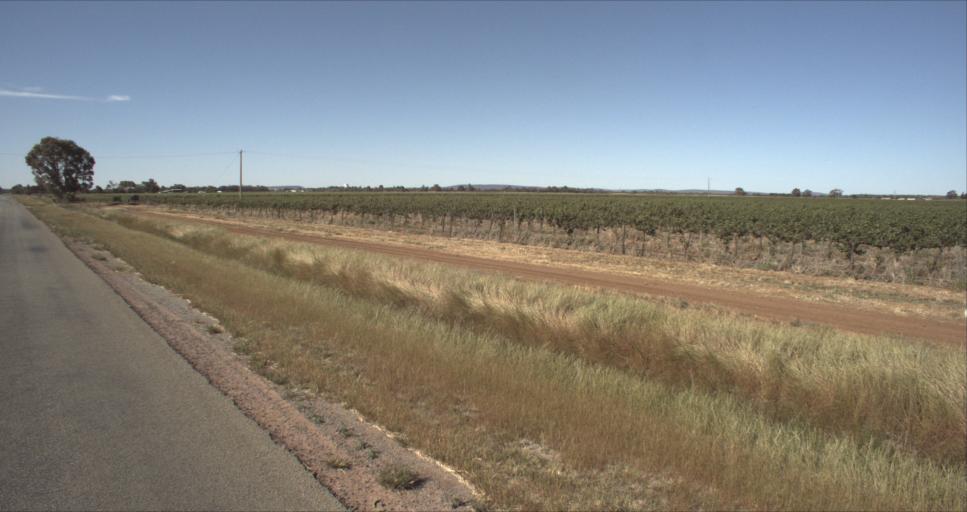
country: AU
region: New South Wales
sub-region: Leeton
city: Leeton
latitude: -34.5794
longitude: 146.3801
